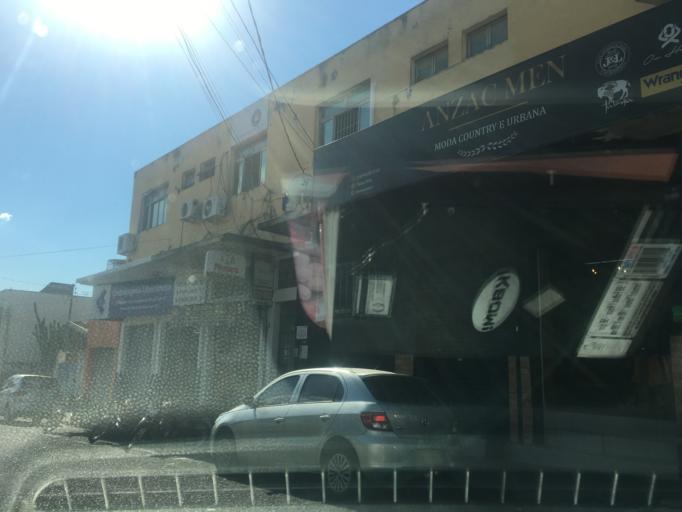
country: BR
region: Minas Gerais
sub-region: Uberlandia
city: Uberlandia
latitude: -18.9147
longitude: -48.2780
